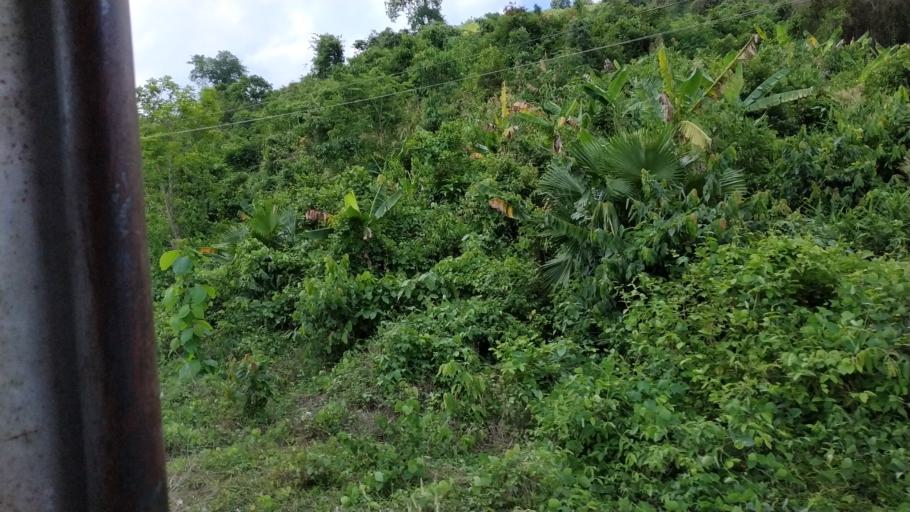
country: MM
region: Mon
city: Kyaikto
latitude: 17.4135
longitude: 97.0725
